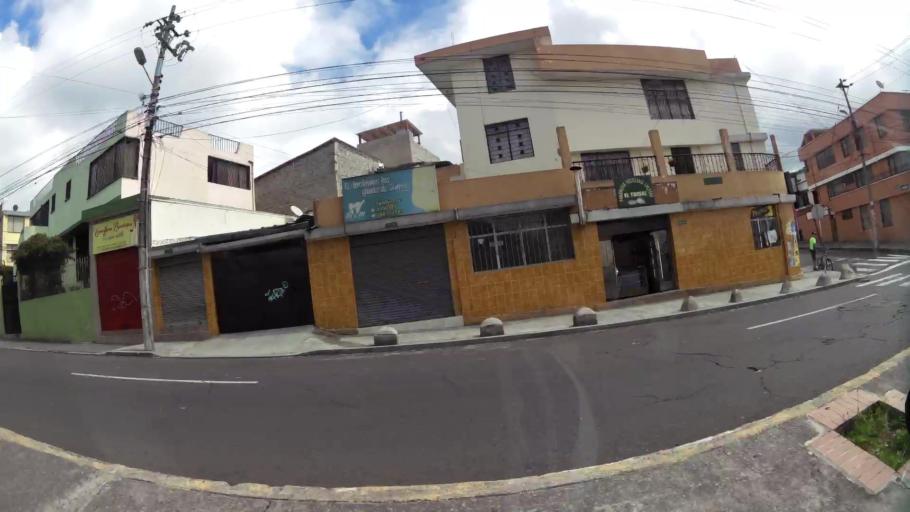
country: EC
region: Pichincha
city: Quito
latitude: -0.1441
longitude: -78.4976
